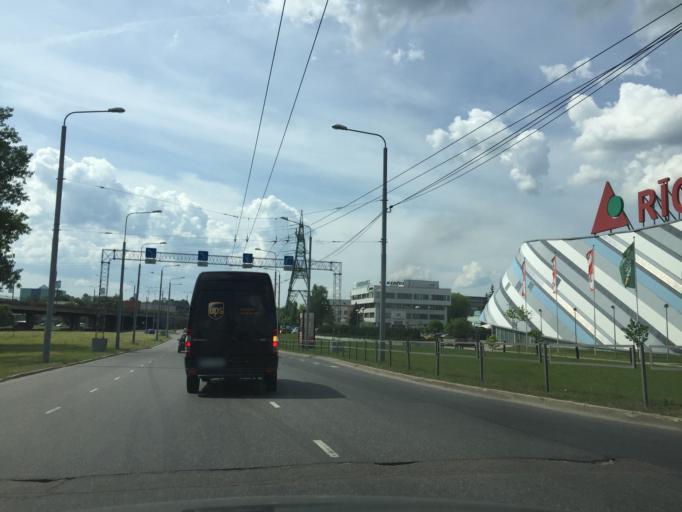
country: LV
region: Riga
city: Riga
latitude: 56.9259
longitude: 24.1069
